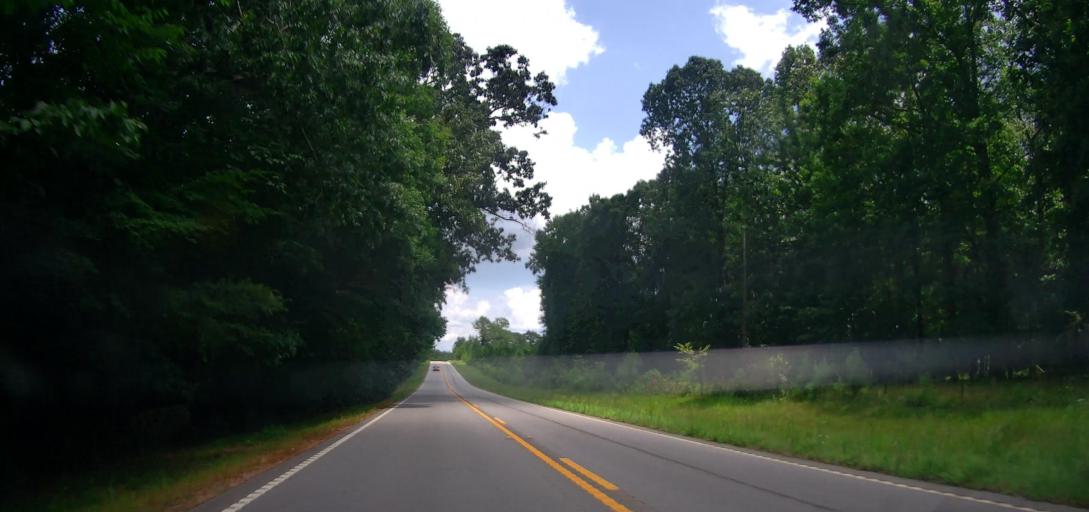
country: US
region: Georgia
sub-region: Meriwether County
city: Greenville
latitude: 33.0116
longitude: -84.6635
